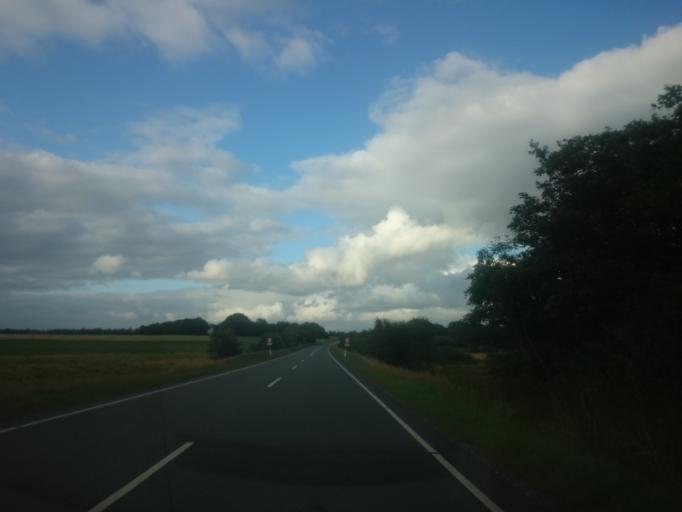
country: DK
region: South Denmark
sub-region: Varde Kommune
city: Olgod
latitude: 55.6648
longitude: 8.7076
